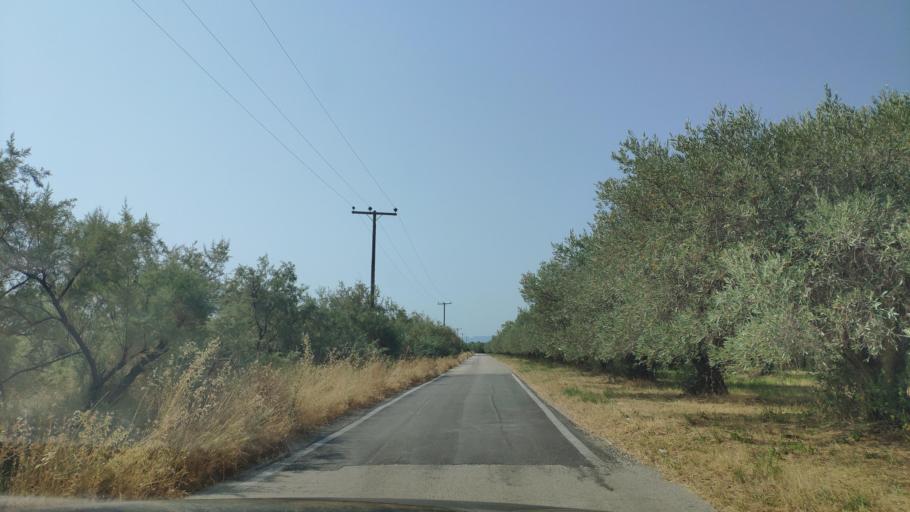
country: GR
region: West Greece
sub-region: Nomos Aitolias kai Akarnanias
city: Menidi
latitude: 39.0476
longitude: 21.0722
